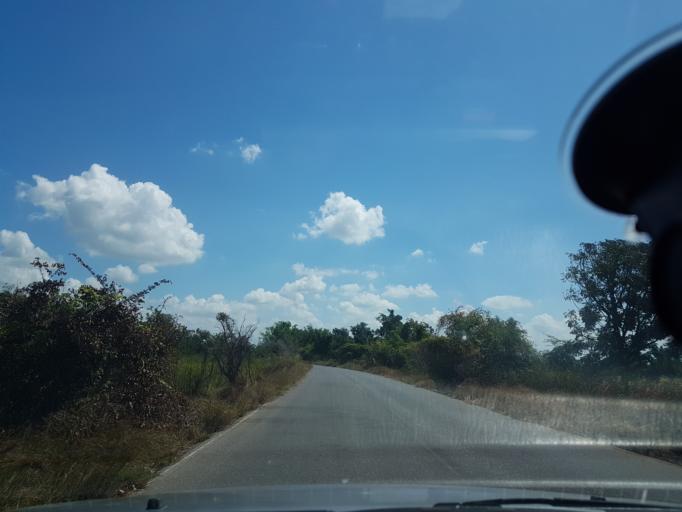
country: TH
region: Lop Buri
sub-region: Amphoe Tha Luang
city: Tha Luang
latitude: 15.0050
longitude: 101.0000
